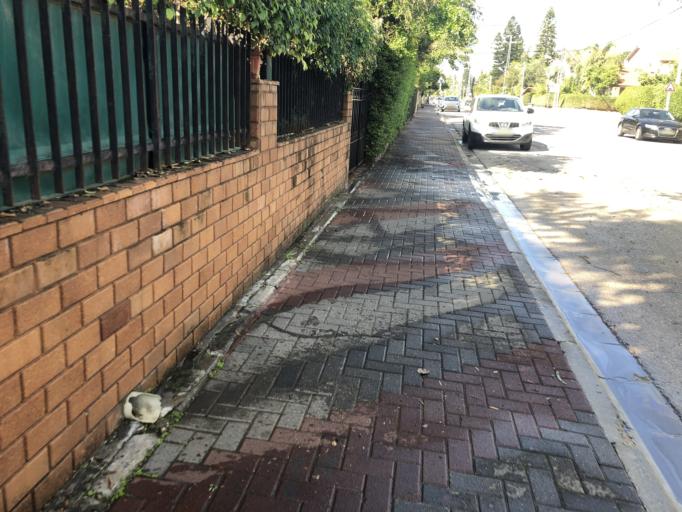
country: IL
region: Central District
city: Yehud
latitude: 32.0292
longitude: 34.8761
